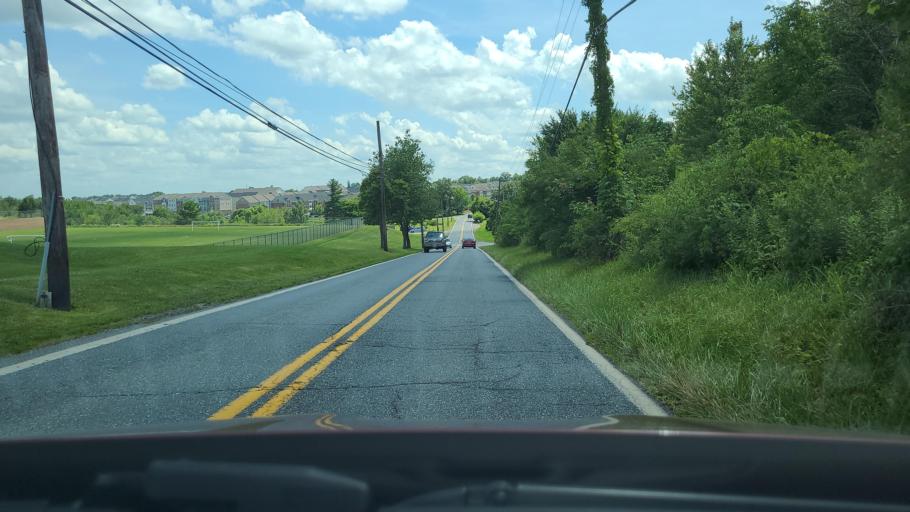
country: US
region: Maryland
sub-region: Montgomery County
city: Clarksburg
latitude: 39.2478
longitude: -77.2769
